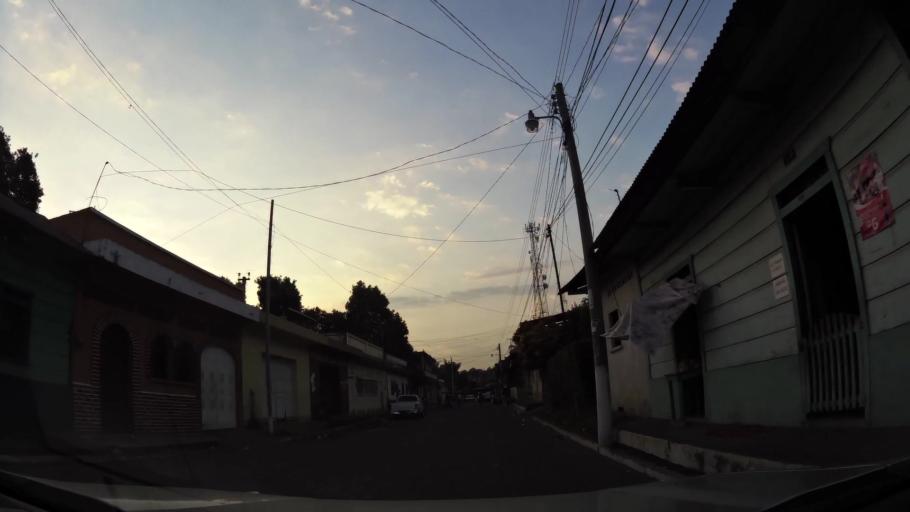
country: GT
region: Retalhuleu
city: San Sebastian
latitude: 14.5641
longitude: -91.6505
